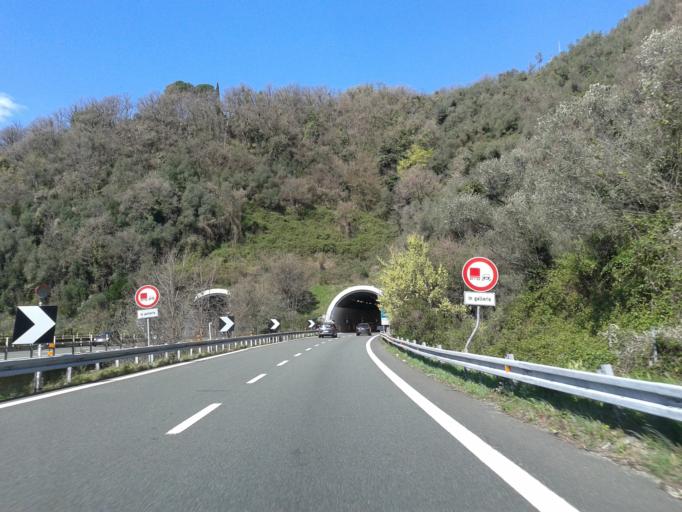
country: IT
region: Liguria
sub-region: Provincia di Genova
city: Moneglia
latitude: 44.2551
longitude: 9.4896
